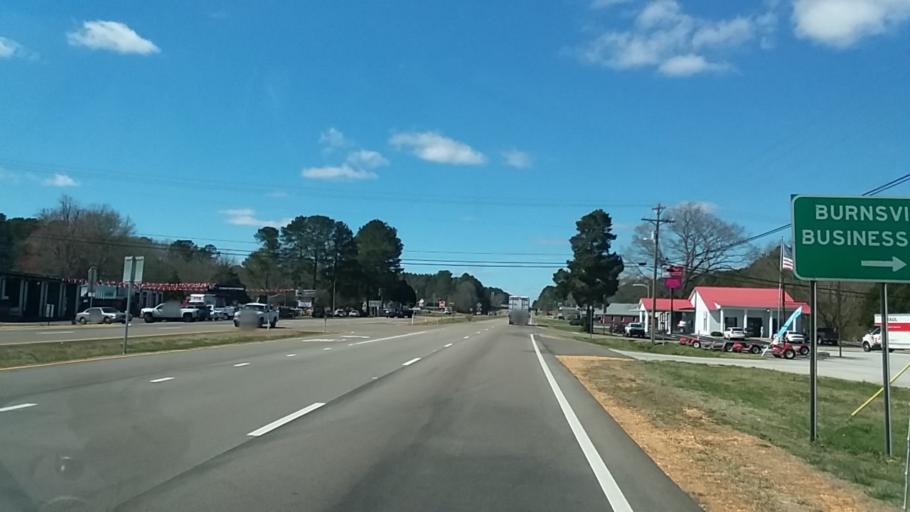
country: US
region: Mississippi
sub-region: Tishomingo County
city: Iuka
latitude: 34.8354
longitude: -88.3162
